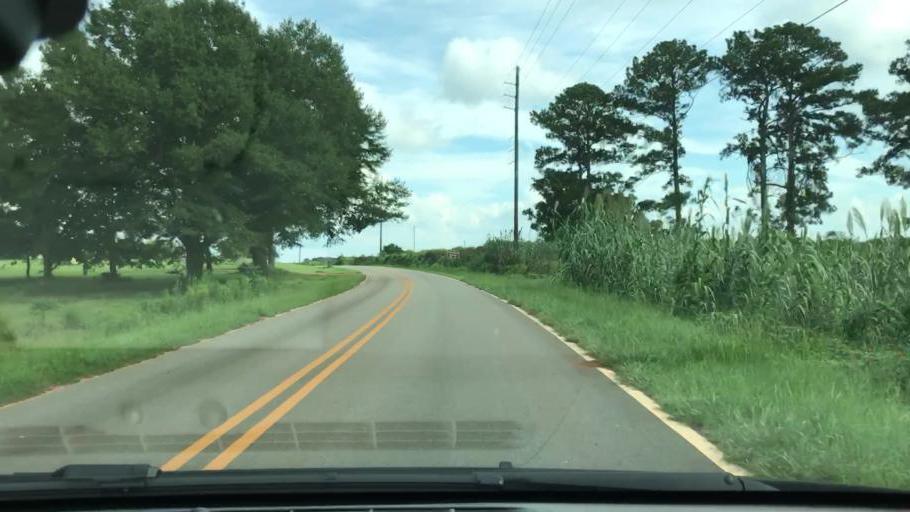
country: US
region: Georgia
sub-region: Clay County
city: Fort Gaines
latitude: 31.5318
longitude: -84.9560
